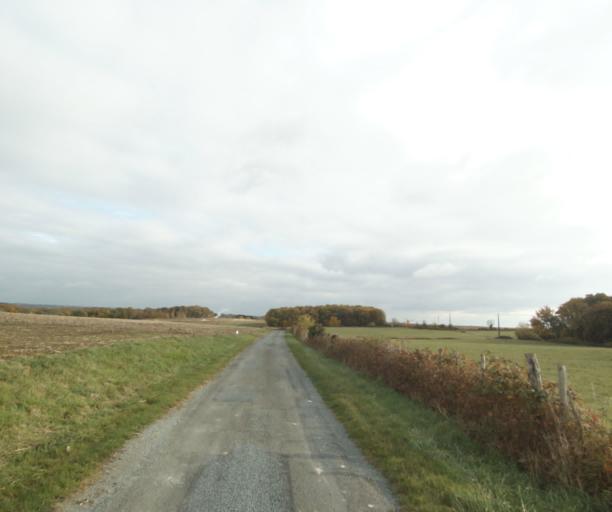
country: FR
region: Poitou-Charentes
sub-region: Departement de la Charente-Maritime
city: Saint-Georges-des-Coteaux
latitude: 45.7640
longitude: -0.6823
